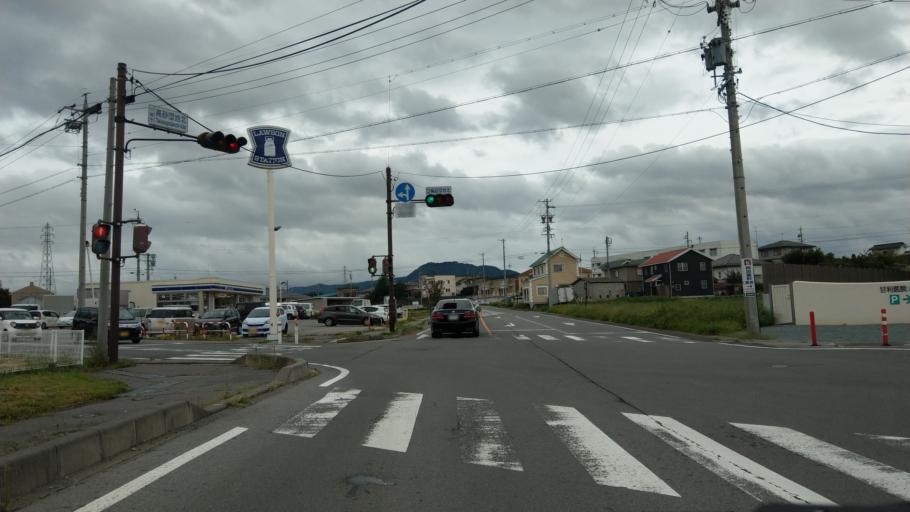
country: JP
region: Nagano
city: Komoro
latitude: 36.2973
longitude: 138.4627
